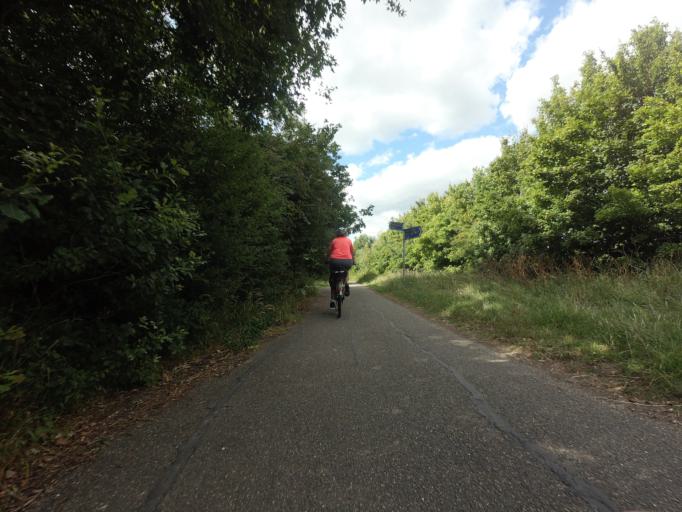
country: GB
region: England
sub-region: East Sussex
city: Eastbourne
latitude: 50.8162
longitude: 0.2756
